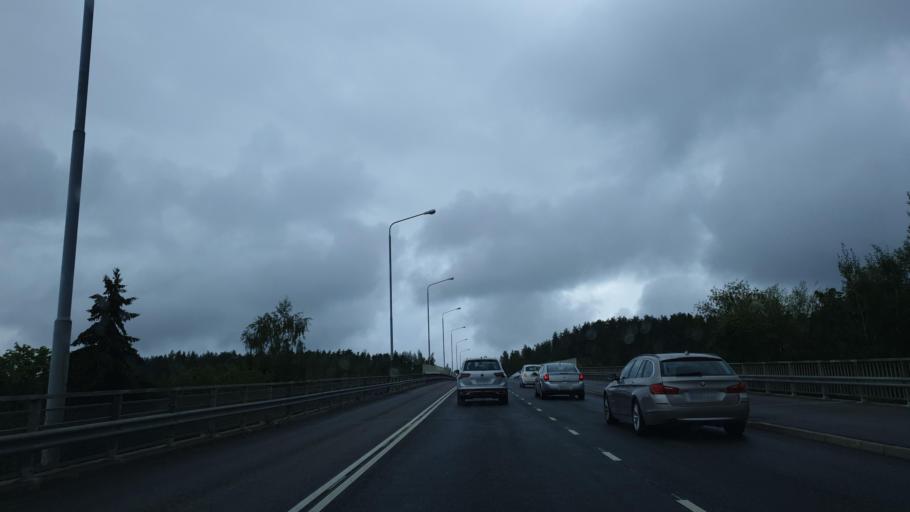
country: FI
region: Paijanne Tavastia
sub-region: Lahti
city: Lahti
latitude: 60.9747
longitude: 25.6754
